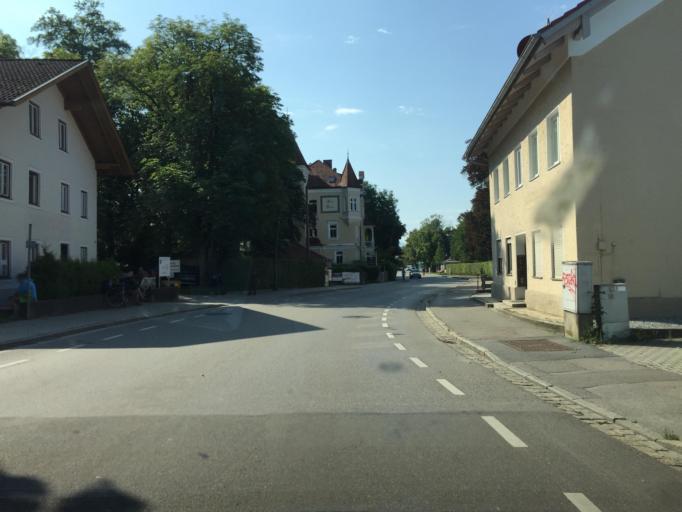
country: DE
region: Bavaria
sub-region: Upper Bavaria
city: Bad Aibling
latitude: 47.8608
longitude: 12.0133
